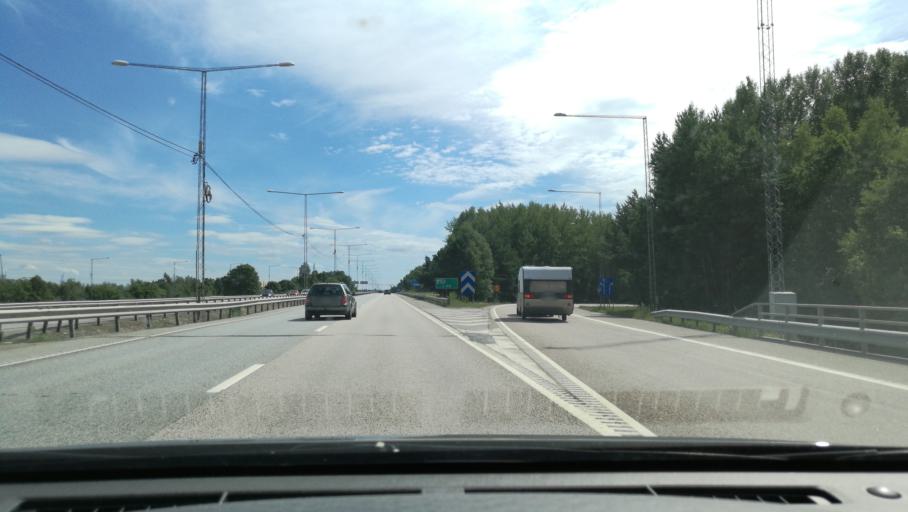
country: SE
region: Stockholm
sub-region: Jarfalla Kommun
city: Jakobsberg
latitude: 59.4223
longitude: 17.8515
